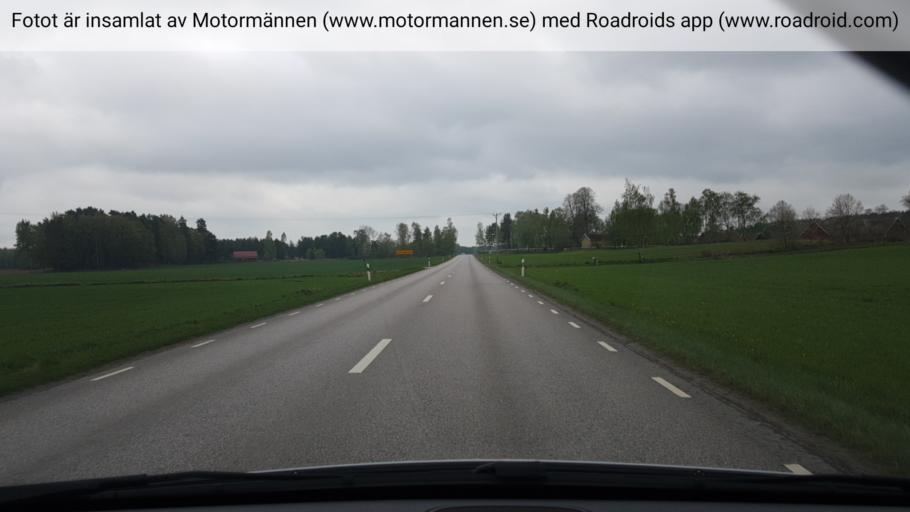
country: SE
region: Vaestra Goetaland
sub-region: Skovde Kommun
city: Stopen
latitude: 58.4843
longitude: 13.9586
